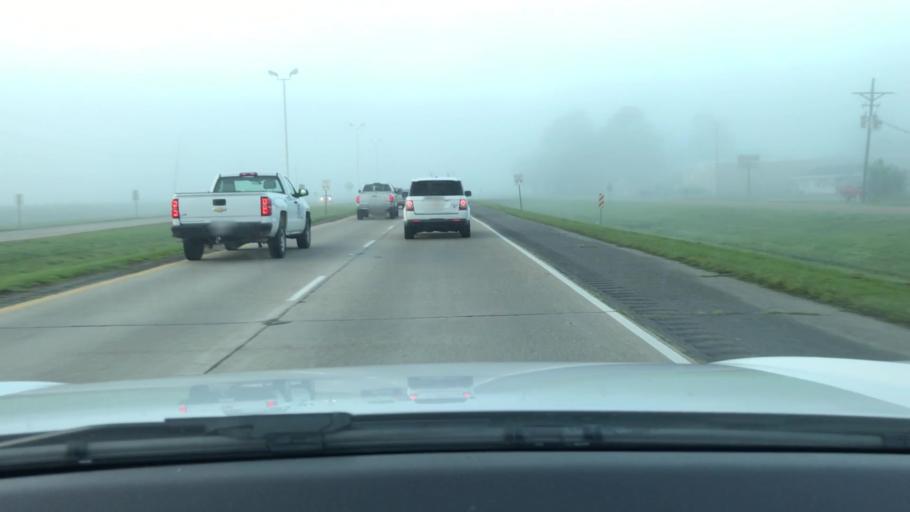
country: US
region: Louisiana
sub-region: West Baton Rouge Parish
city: Addis
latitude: 30.3546
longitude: -91.2592
